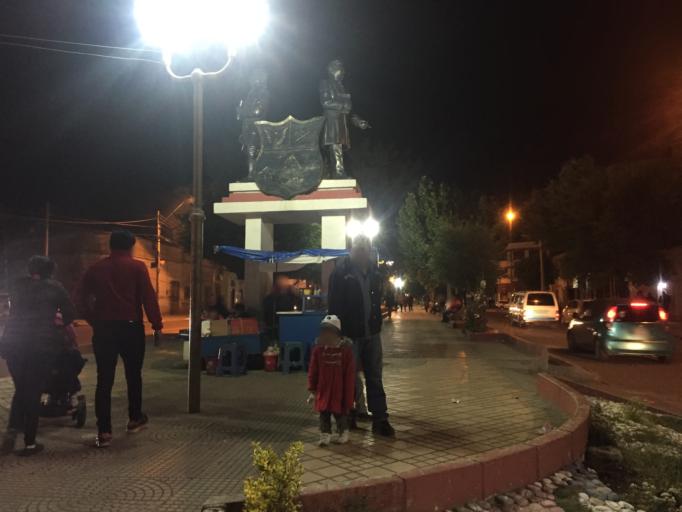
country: BO
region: Oruro
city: Oruro
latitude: -17.9508
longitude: -67.1111
